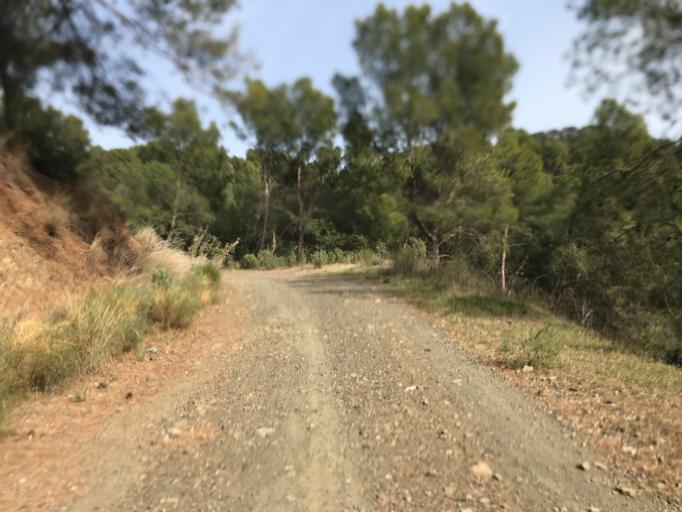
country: ES
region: Andalusia
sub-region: Provincia de Malaga
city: Malaga
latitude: 36.8022
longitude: -4.4057
